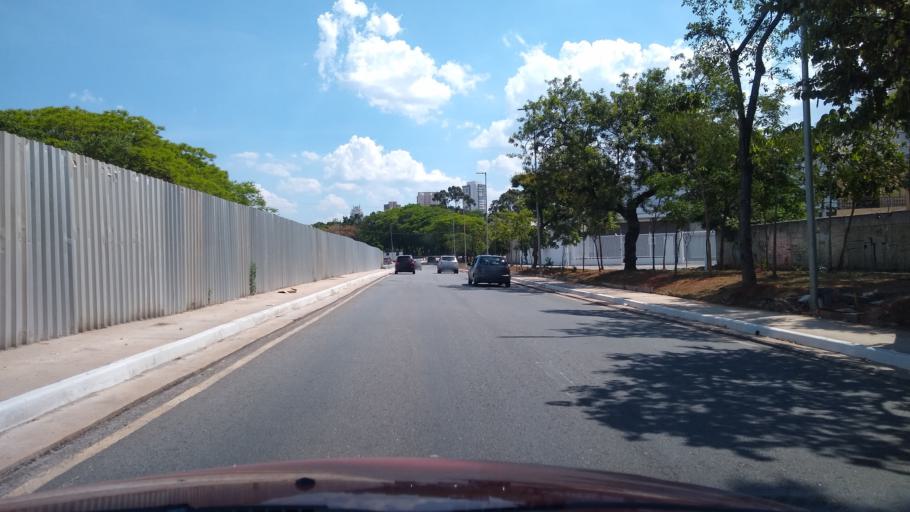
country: BR
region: Sao Paulo
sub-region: Diadema
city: Diadema
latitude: -23.6274
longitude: -46.6300
